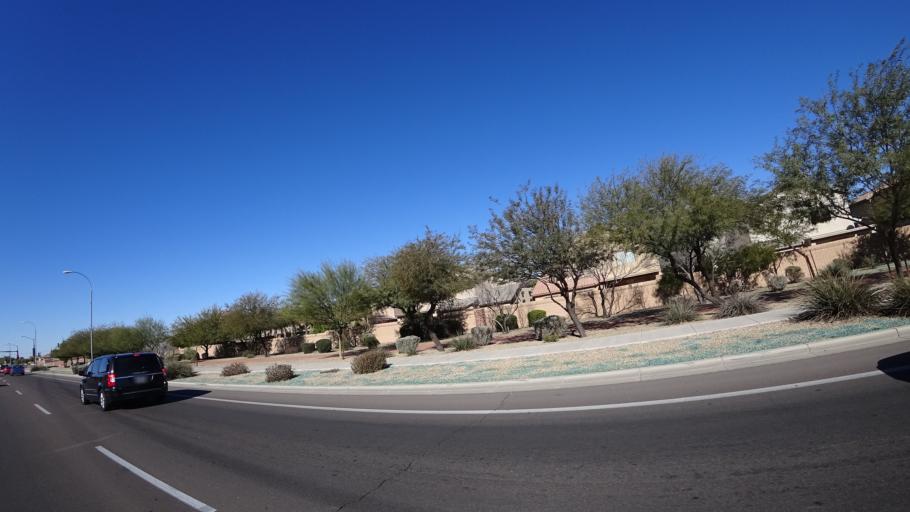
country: US
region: Arizona
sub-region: Maricopa County
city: Laveen
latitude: 33.3776
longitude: -112.1578
